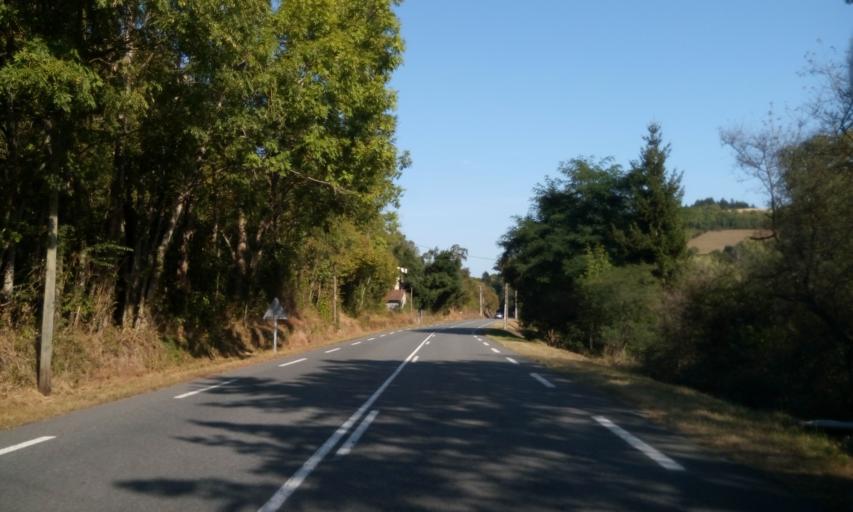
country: FR
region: Rhone-Alpes
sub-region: Departement du Rhone
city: Tarare
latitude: 45.9225
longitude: 4.4663
